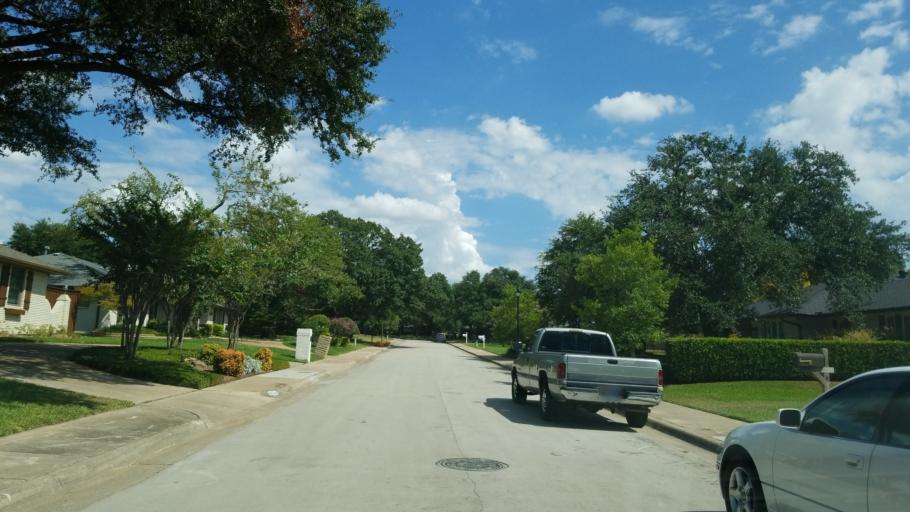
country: US
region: Texas
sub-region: Dallas County
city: Addison
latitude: 32.9550
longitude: -96.7906
